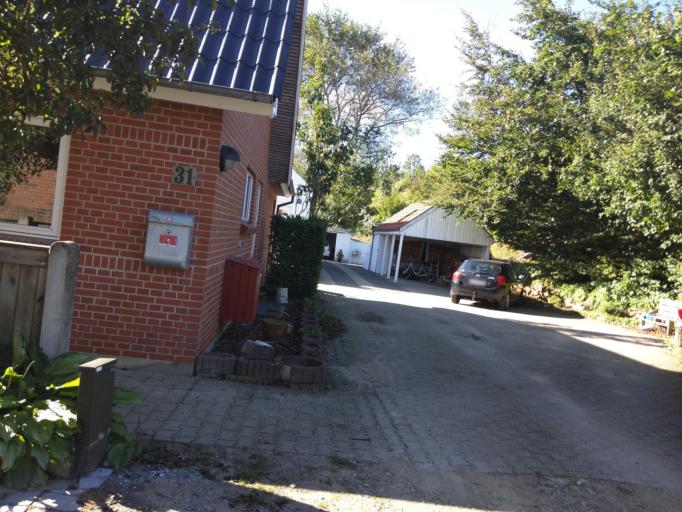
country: DK
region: Central Jutland
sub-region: Viborg Kommune
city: Viborg
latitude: 56.4383
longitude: 9.3998
